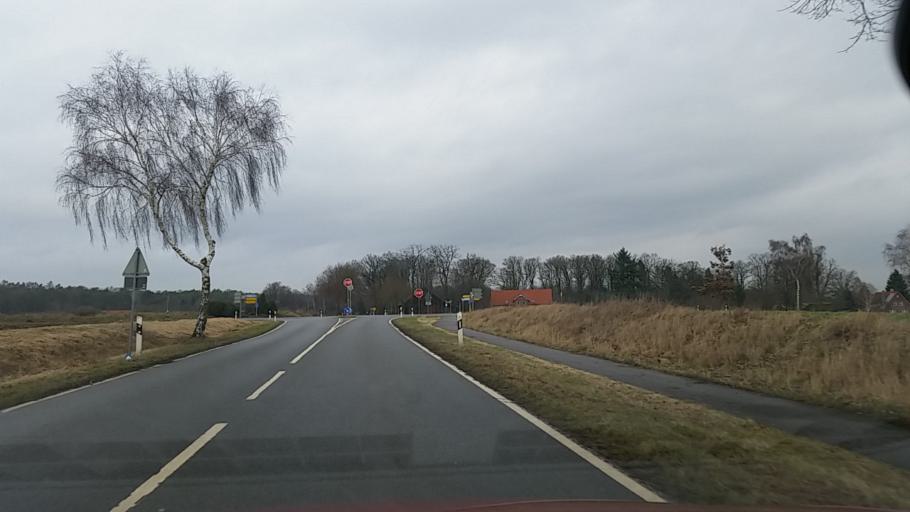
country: DE
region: Lower Saxony
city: Bispingen
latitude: 53.1262
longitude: 9.9995
